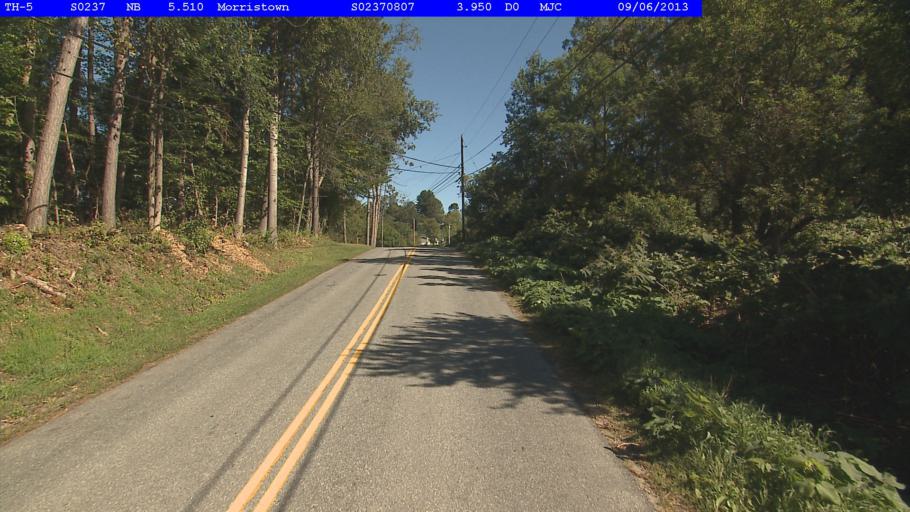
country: US
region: Vermont
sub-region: Lamoille County
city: Morristown
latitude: 44.5534
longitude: -72.6260
